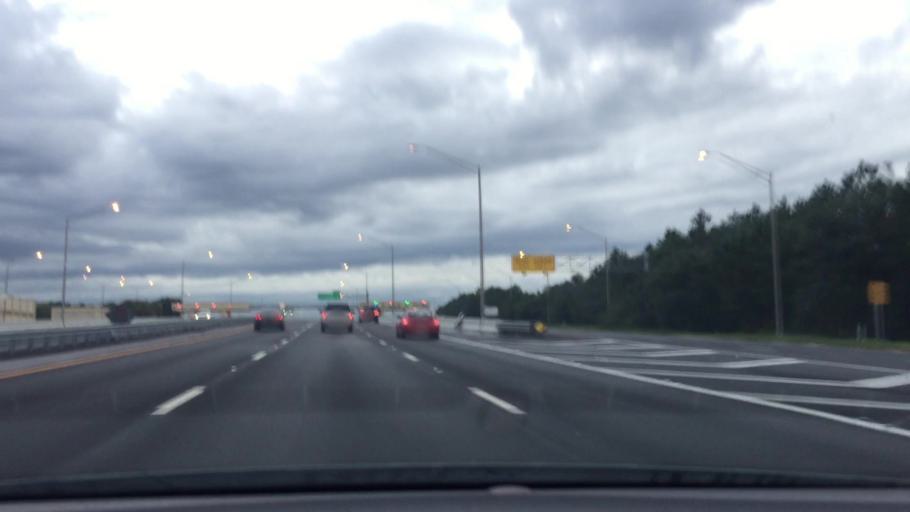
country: US
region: Florida
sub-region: Orange County
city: Orlovista
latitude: 28.5490
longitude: -81.4889
